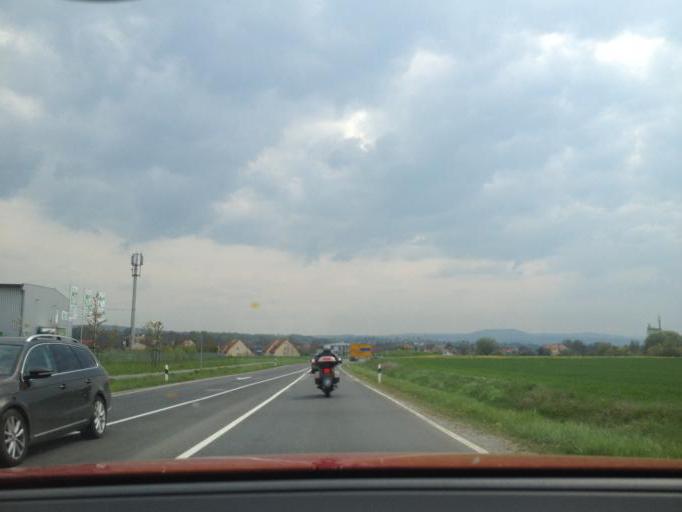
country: DE
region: Bavaria
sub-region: Upper Franconia
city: Bindlach
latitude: 49.9656
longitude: 11.6257
